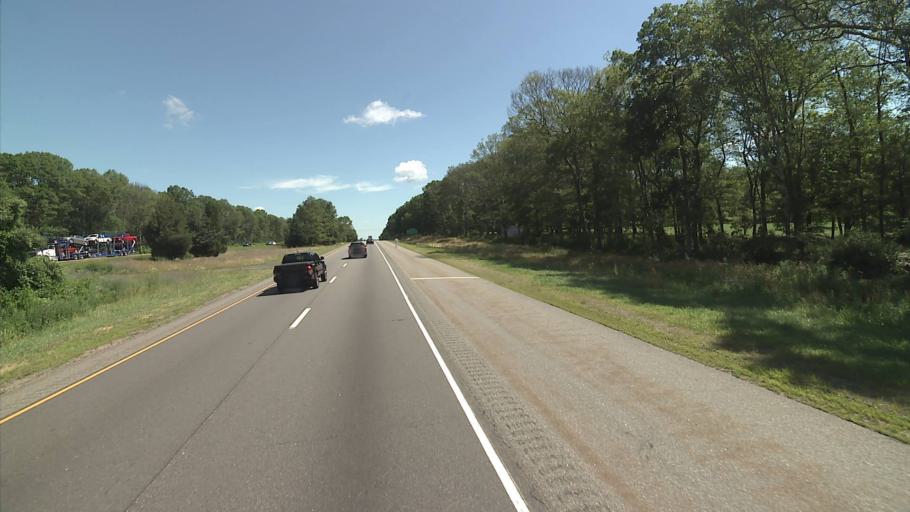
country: US
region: Connecticut
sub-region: New London County
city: Pawcatuck
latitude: 41.4019
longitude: -71.8626
